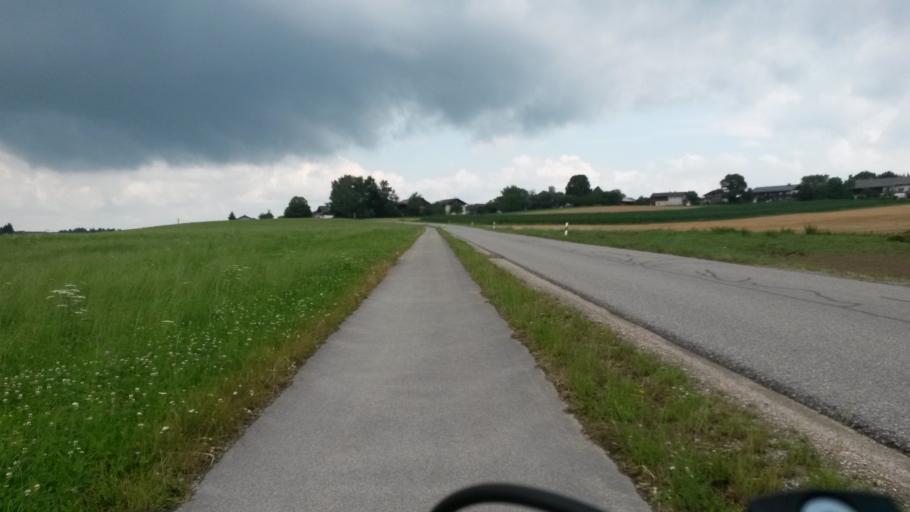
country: DE
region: Bavaria
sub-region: Upper Bavaria
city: Hoslwang
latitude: 47.9621
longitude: 12.3253
